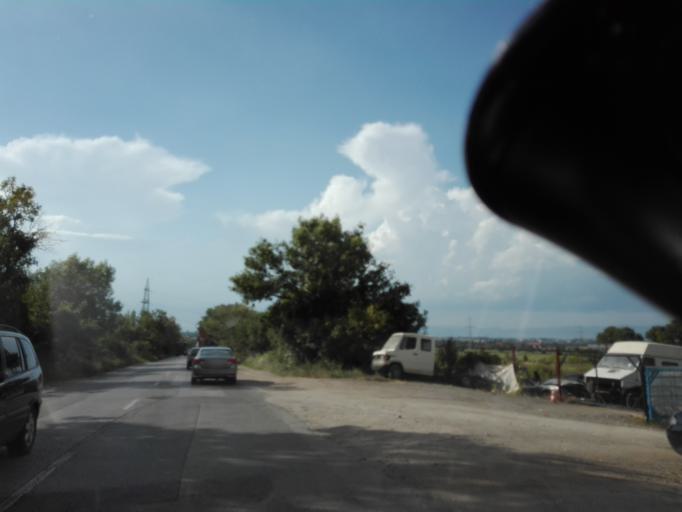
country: BG
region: Sofiya
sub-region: Obshtina Elin Pelin
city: Elin Pelin
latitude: 42.6164
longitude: 23.4580
